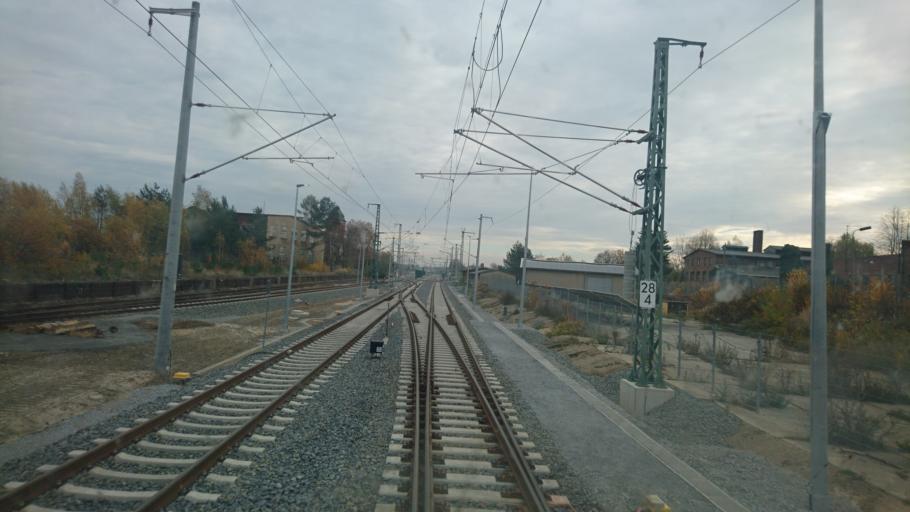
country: DE
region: Saxony
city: Niesky
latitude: 51.2998
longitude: 14.8232
